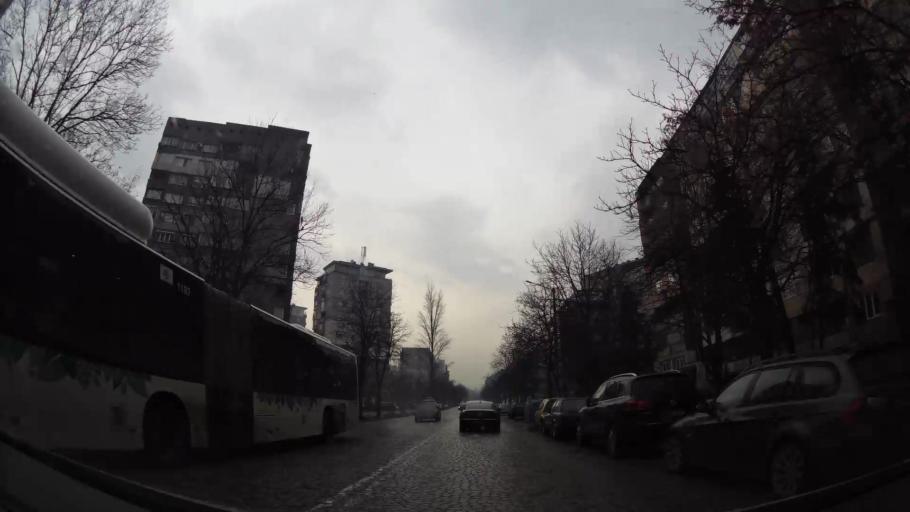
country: BG
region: Sofia-Capital
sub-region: Stolichna Obshtina
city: Sofia
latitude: 42.6688
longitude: 23.2982
